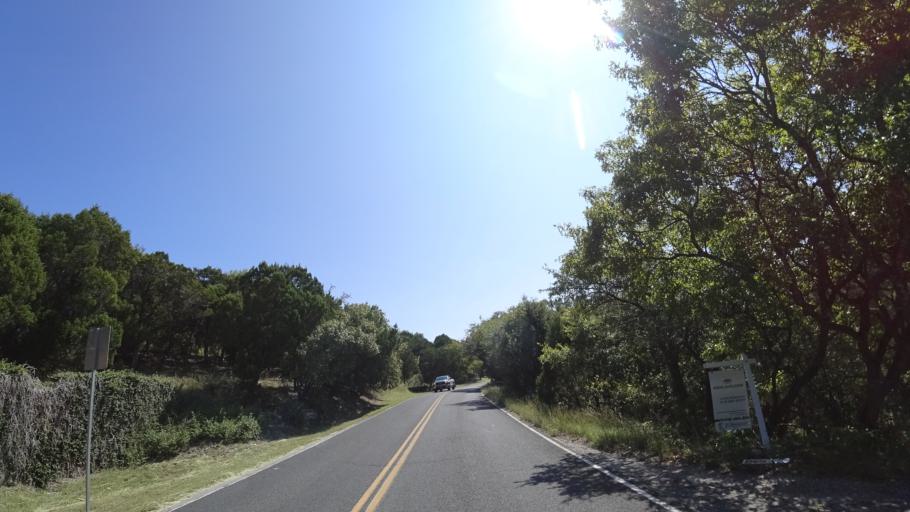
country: US
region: Texas
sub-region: Travis County
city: West Lake Hills
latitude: 30.3065
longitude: -97.7959
